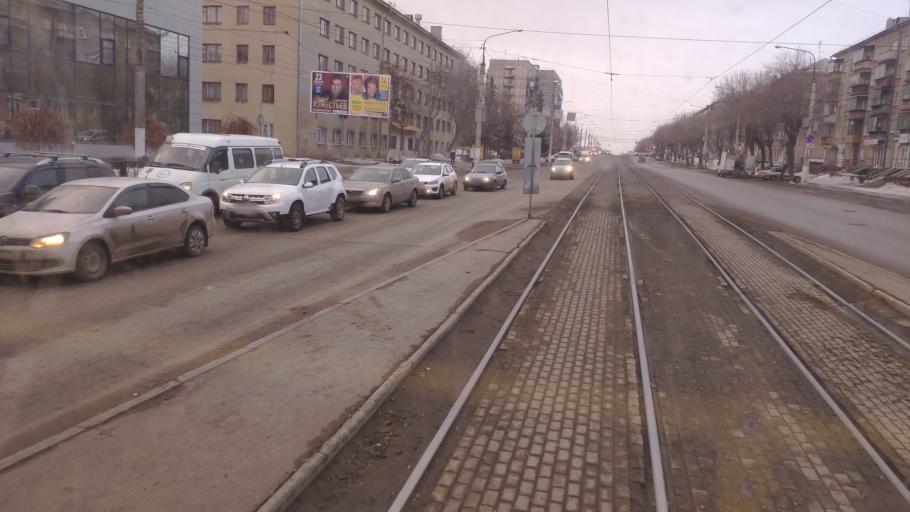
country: RU
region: Chelyabinsk
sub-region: Gorod Magnitogorsk
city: Magnitogorsk
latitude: 53.4111
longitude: 58.9782
